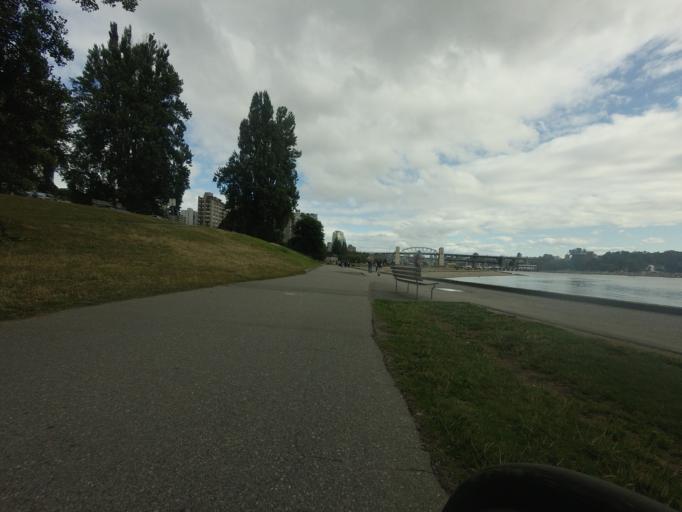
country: CA
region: British Columbia
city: West End
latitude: 49.2811
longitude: -123.1405
